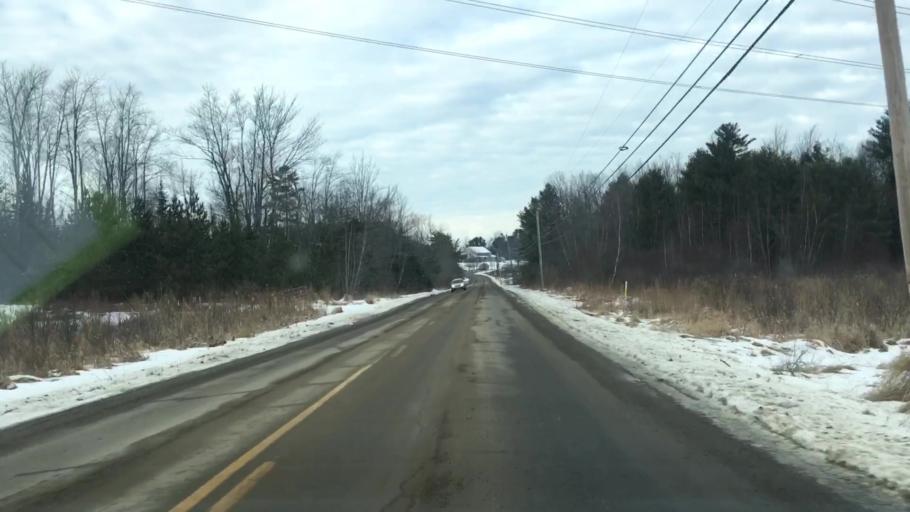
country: US
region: Maine
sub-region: Lincoln County
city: Whitefield
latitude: 44.2322
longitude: -69.6159
